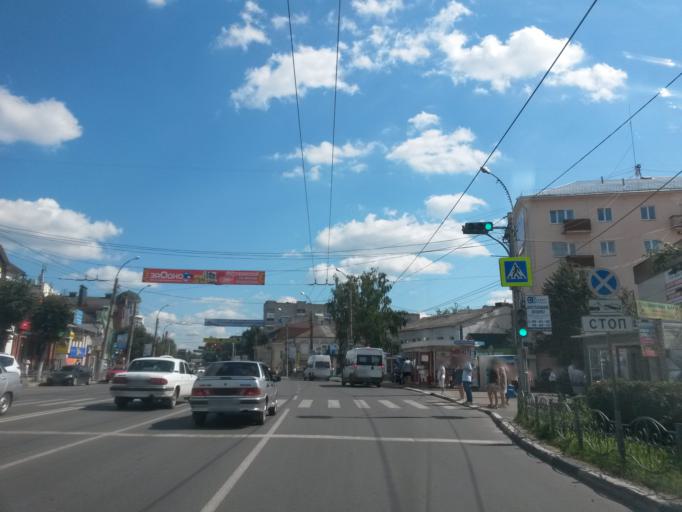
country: RU
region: Ivanovo
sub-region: Gorod Ivanovo
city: Ivanovo
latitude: 56.9954
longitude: 40.9832
